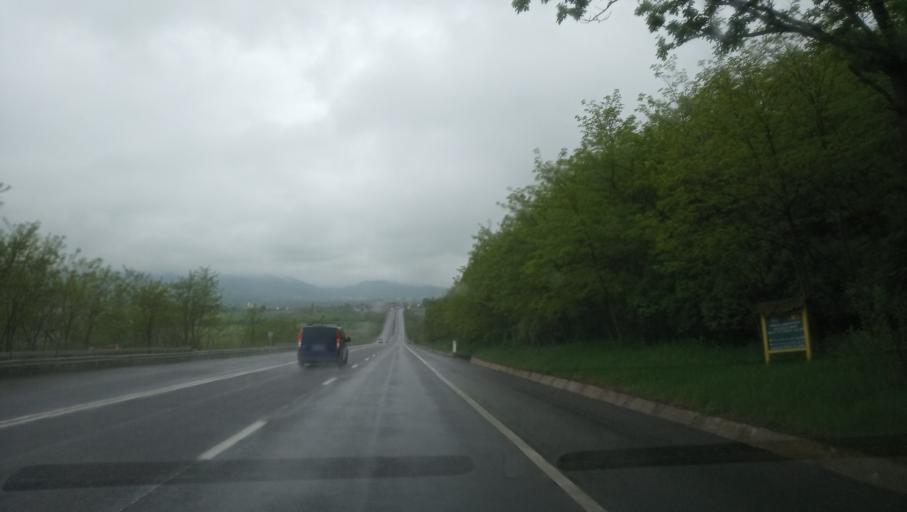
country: RO
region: Sibiu
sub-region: Comuna Orlat
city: Orlat
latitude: 45.7779
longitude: 23.9593
